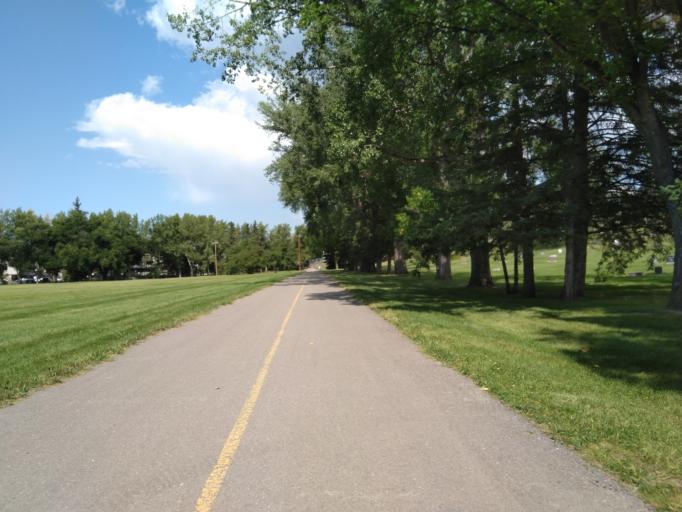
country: CA
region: Alberta
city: Calgary
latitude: 51.0846
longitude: -114.0736
